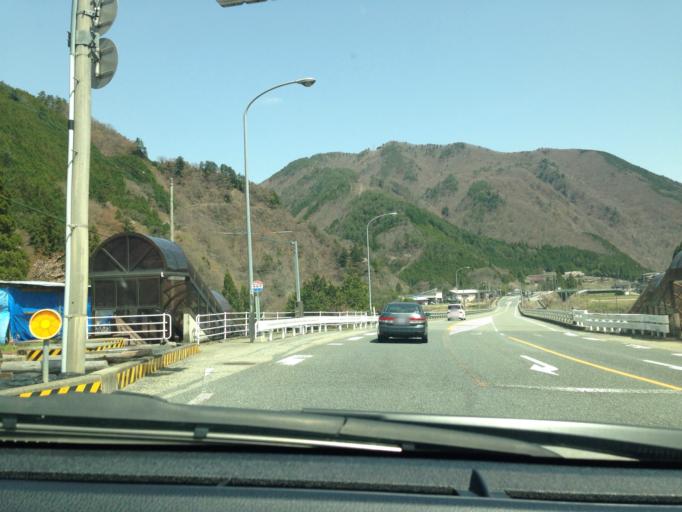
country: JP
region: Gifu
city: Takayama
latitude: 35.9665
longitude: 137.2597
